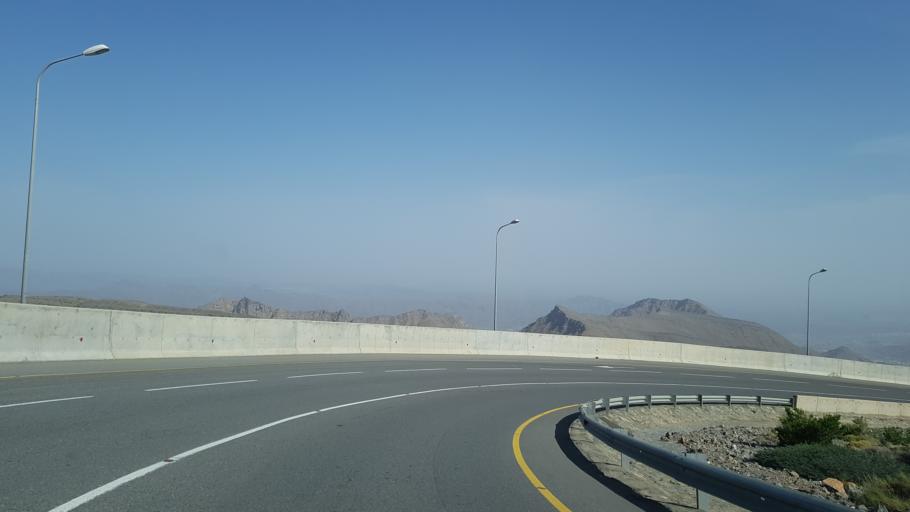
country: OM
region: Muhafazat ad Dakhiliyah
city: Izki
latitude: 23.0053
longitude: 57.7001
